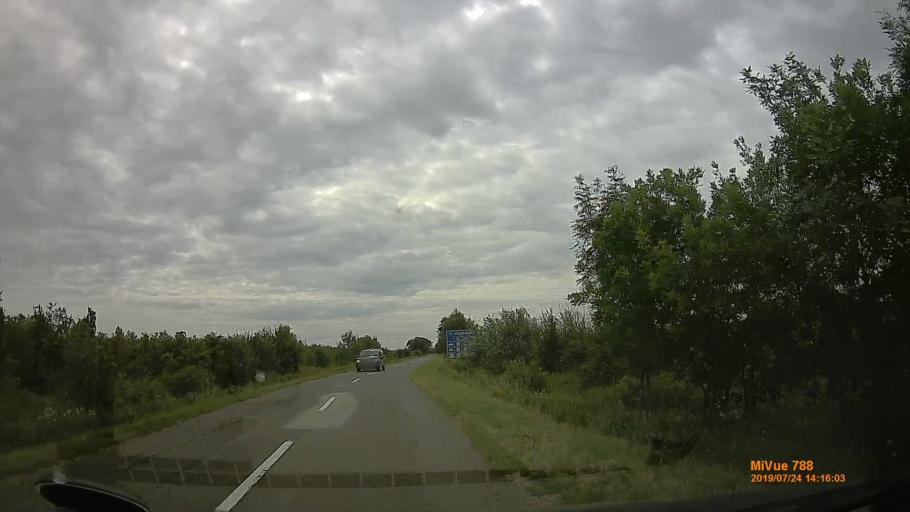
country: HU
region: Szabolcs-Szatmar-Bereg
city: Mandok
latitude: 48.3186
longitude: 22.2994
